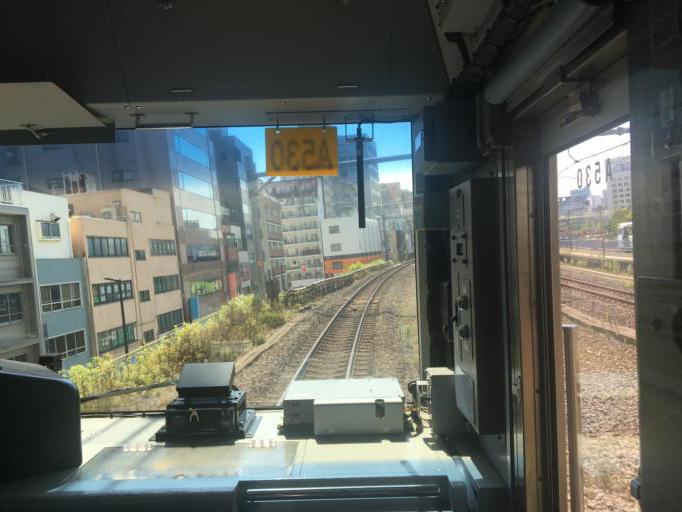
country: JP
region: Tokyo
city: Urayasu
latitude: 35.6956
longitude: 139.7961
